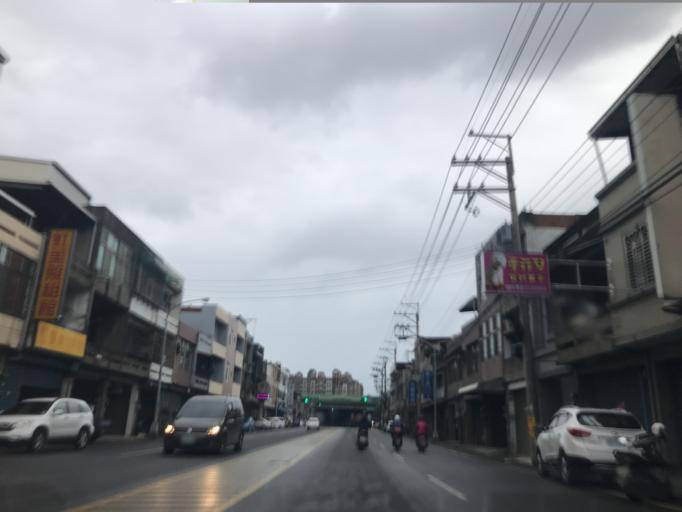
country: TW
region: Taiwan
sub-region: Hsinchu
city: Zhubei
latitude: 24.8344
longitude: 121.0240
